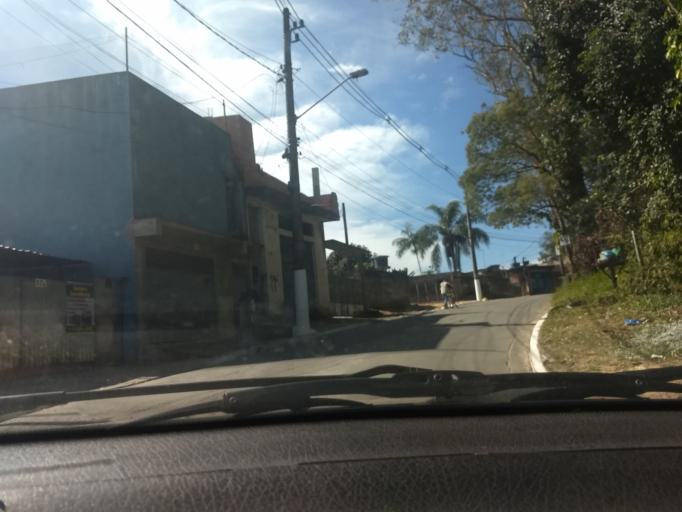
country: BR
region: Sao Paulo
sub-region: Embu-Guacu
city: Embu Guacu
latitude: -23.8250
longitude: -46.7095
